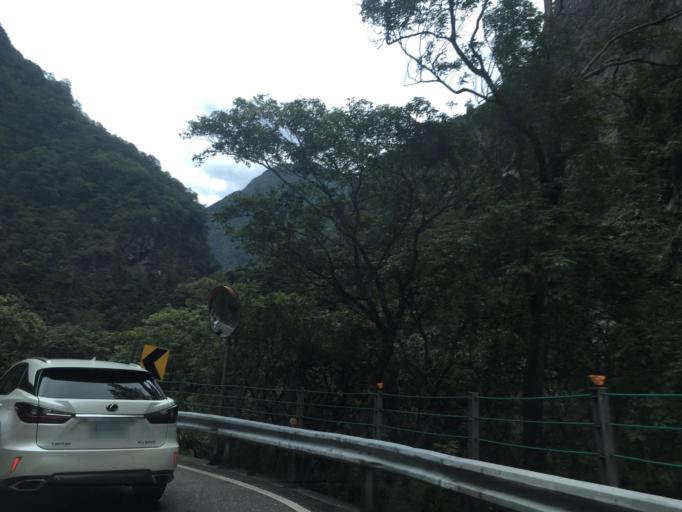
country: TW
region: Taiwan
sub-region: Hualien
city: Hualian
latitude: 24.1736
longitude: 121.5221
